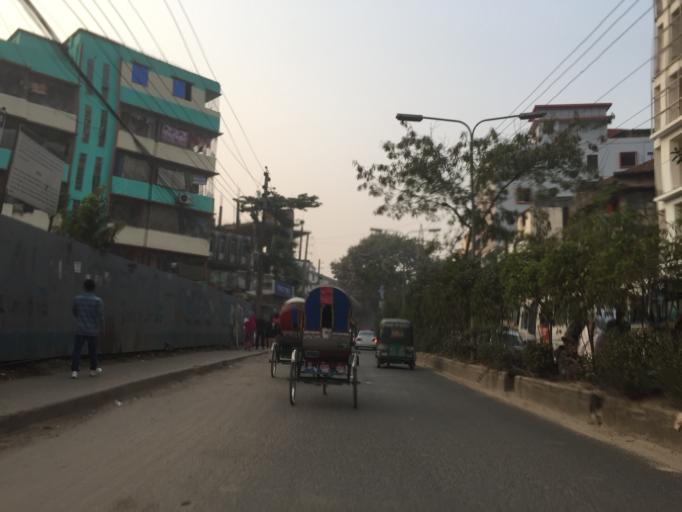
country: BD
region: Dhaka
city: Azimpur
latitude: 23.7564
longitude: 90.3623
